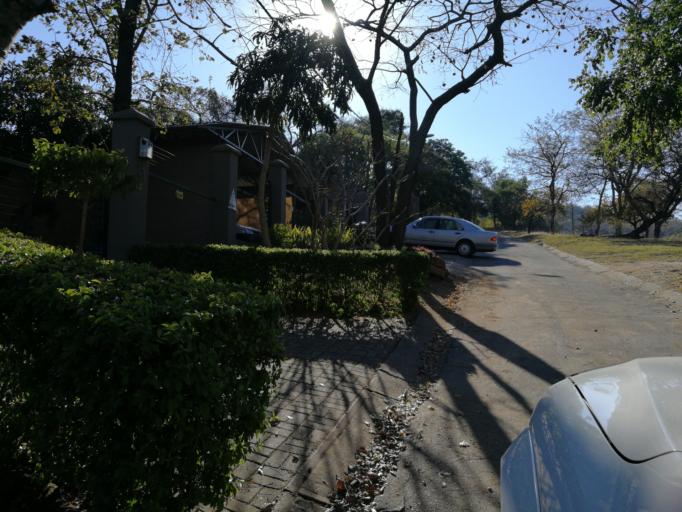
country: ZA
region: Mpumalanga
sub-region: Ehlanzeni District
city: White River
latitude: -25.0651
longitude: 31.1142
